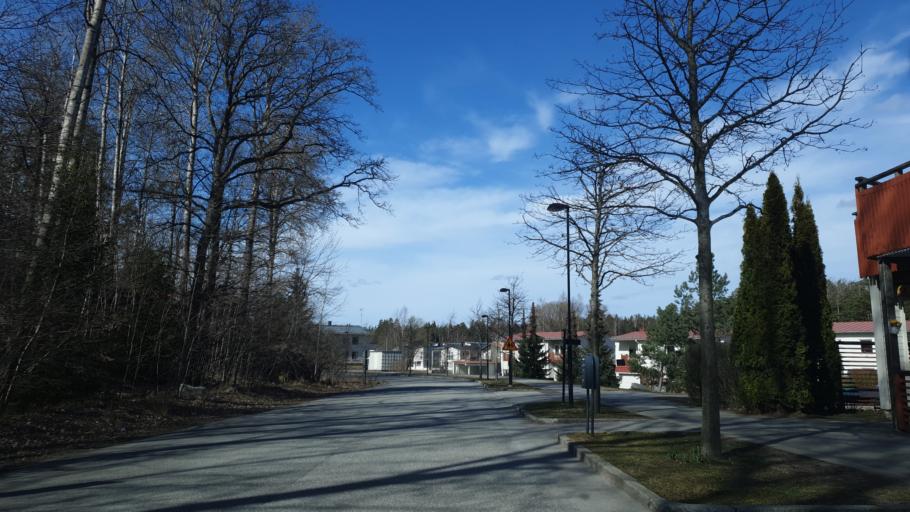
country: SE
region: Stockholm
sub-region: Solna Kommun
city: Rasunda
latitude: 59.3990
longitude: 17.9928
